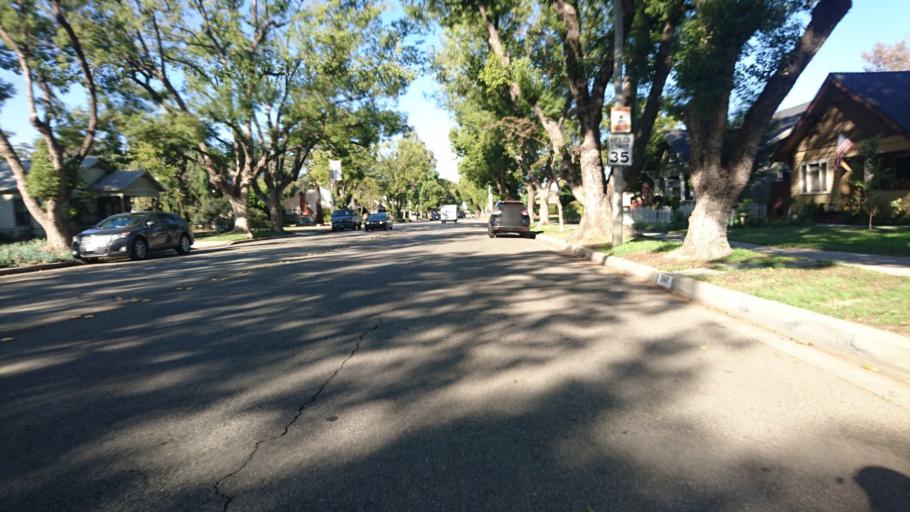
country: US
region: California
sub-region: Los Angeles County
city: La Verne
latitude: 34.0999
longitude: -117.7633
